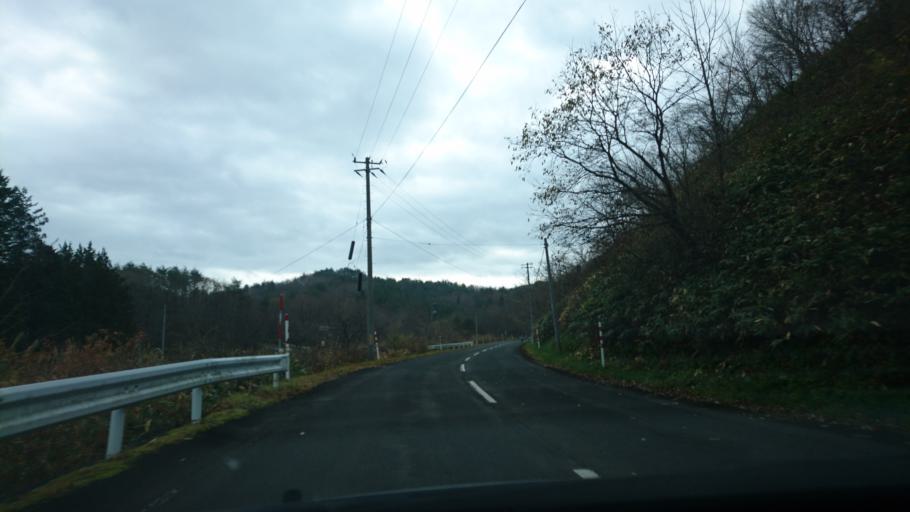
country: JP
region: Iwate
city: Ichinoseki
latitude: 38.9284
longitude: 140.9222
